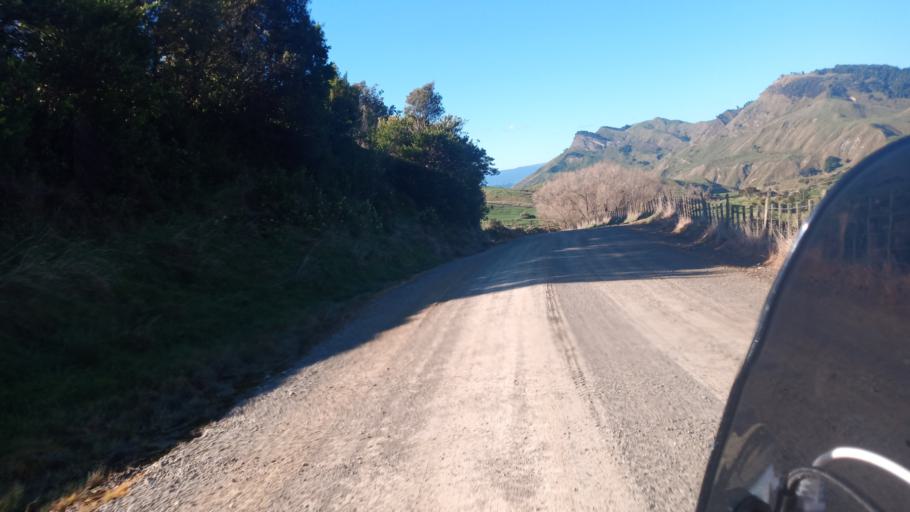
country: NZ
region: Hawke's Bay
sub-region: Wairoa District
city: Wairoa
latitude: -38.7394
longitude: 177.2885
